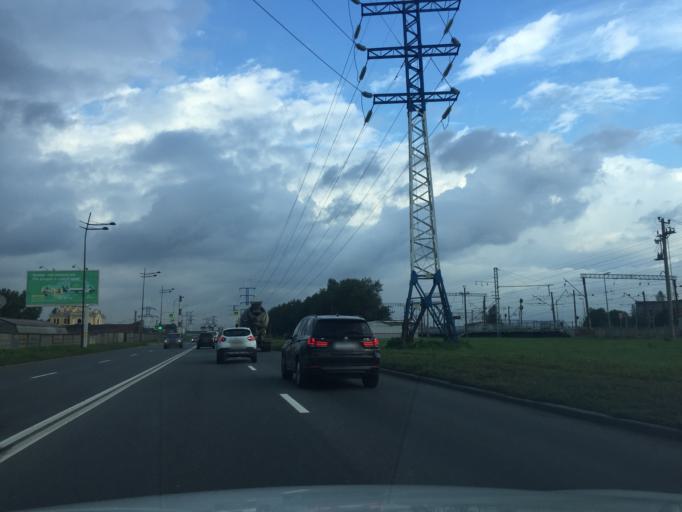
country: RU
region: St.-Petersburg
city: Kupchino
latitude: 59.8905
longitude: 30.3450
